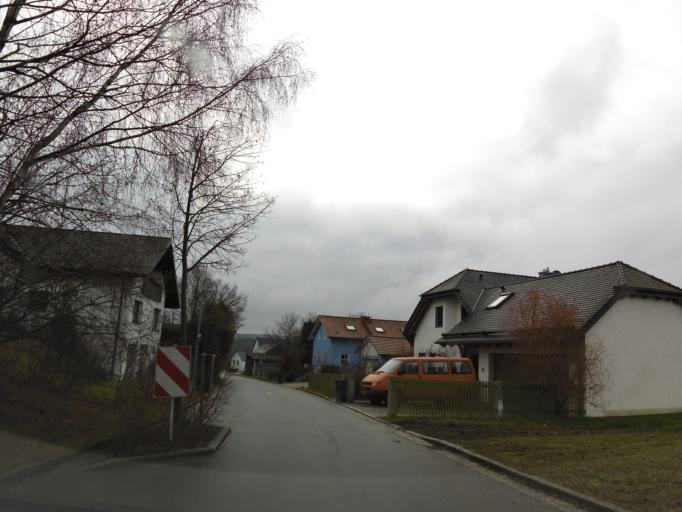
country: DE
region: Bavaria
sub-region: Upper Franconia
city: Wunsiedel
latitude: 50.0471
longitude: 12.0251
